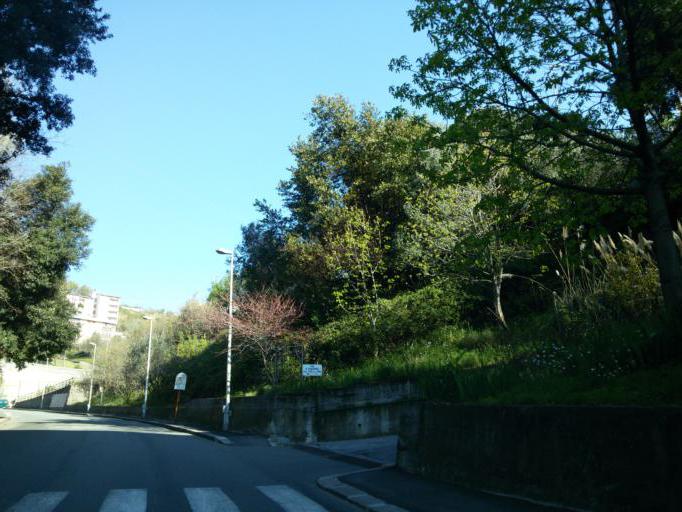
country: IT
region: Liguria
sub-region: Provincia di Genova
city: Genoa
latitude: 44.4257
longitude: 8.9086
